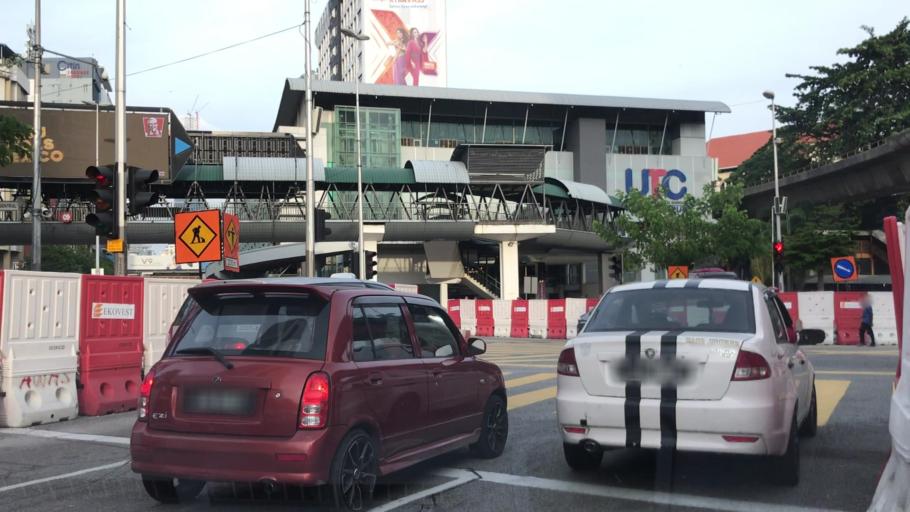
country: MY
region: Kuala Lumpur
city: Kuala Lumpur
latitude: 3.1463
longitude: 101.6995
